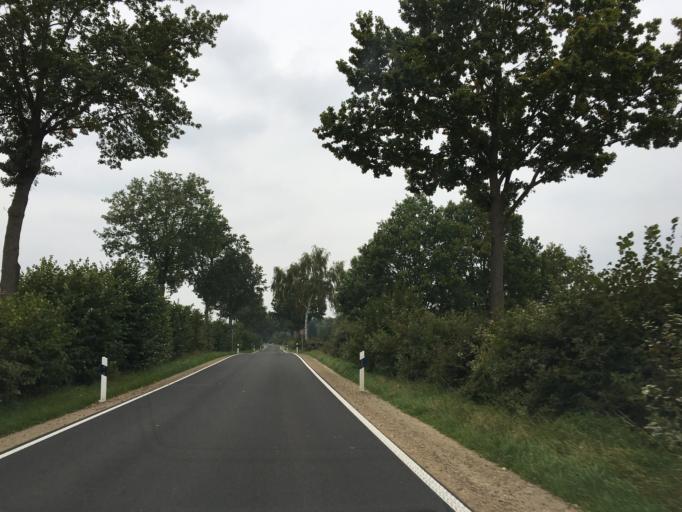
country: DE
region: Schleswig-Holstein
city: Seedorf
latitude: 53.6102
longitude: 10.8886
